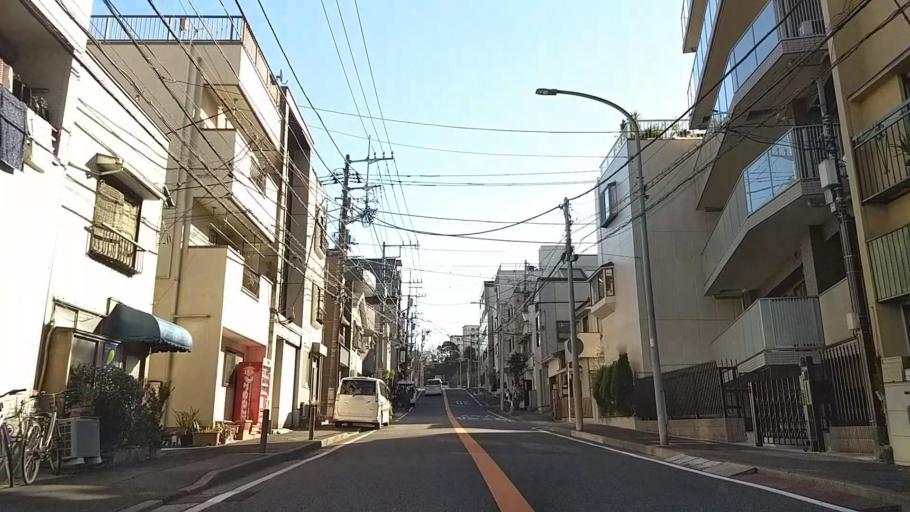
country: JP
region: Kanagawa
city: Yokohama
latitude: 35.4519
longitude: 139.6243
